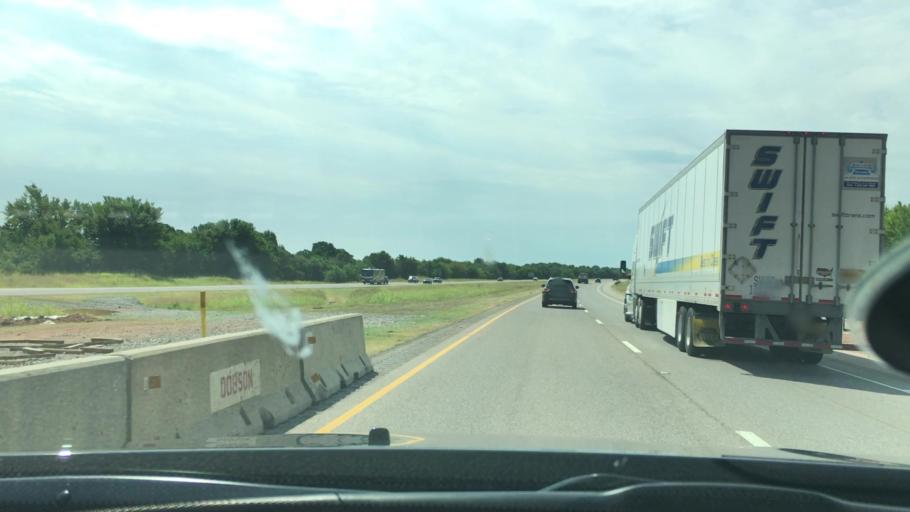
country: US
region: Oklahoma
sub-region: Murray County
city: Davis
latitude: 34.4879
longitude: -97.1614
